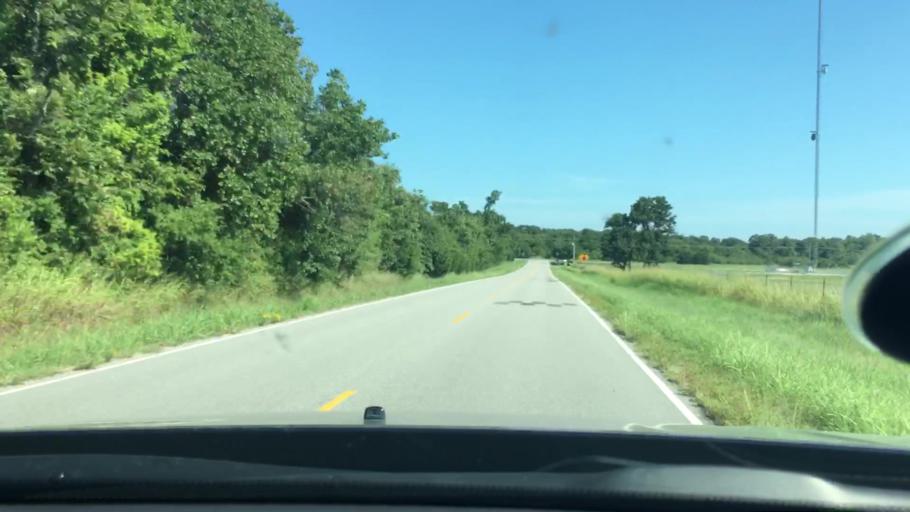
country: US
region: Oklahoma
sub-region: Johnston County
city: Tishomingo
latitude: 34.3581
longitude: -96.5488
